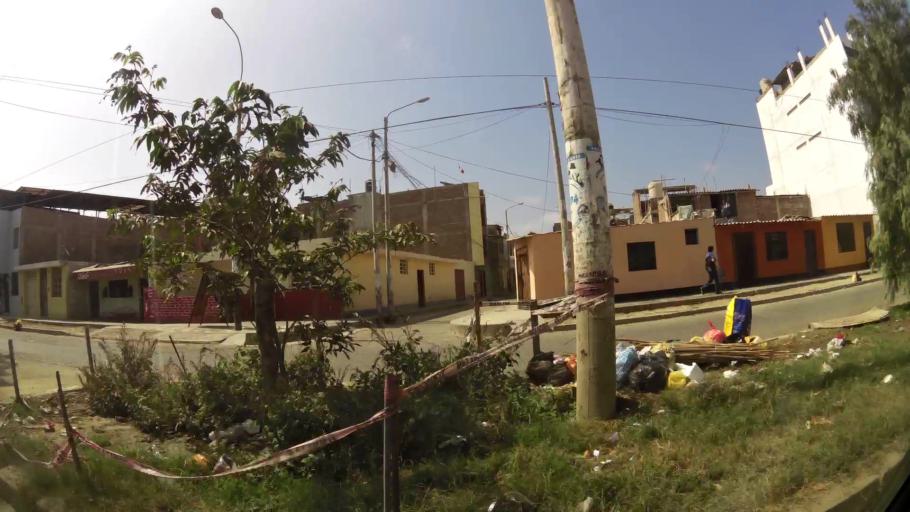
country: PE
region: La Libertad
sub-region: Provincia de Trujillo
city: Buenos Aires
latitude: -8.1335
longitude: -79.0479
